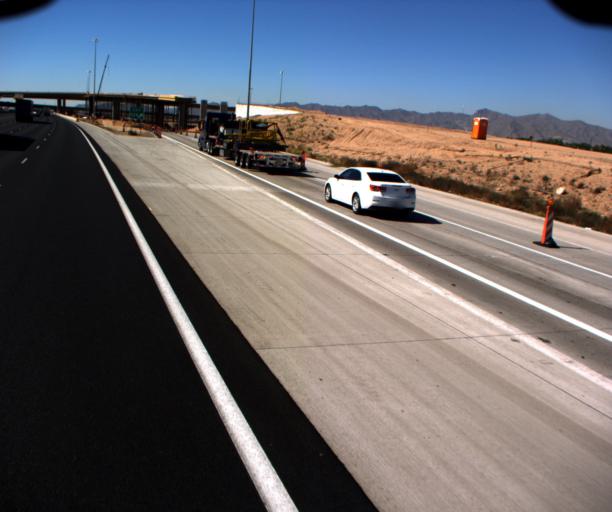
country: US
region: Arizona
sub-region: Maricopa County
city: Goodyear
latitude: 33.4624
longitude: -112.4188
